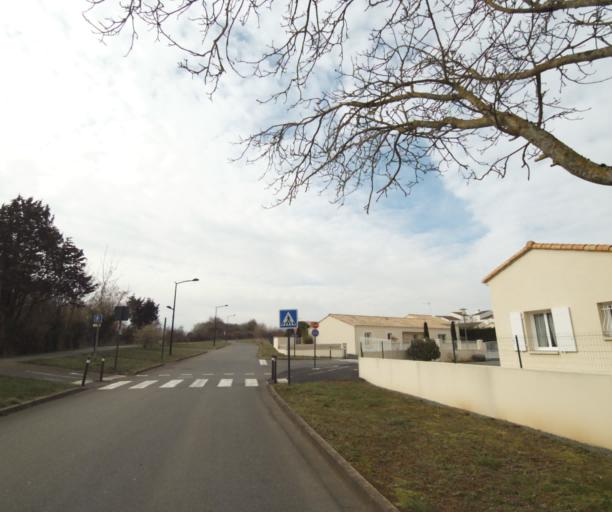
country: FR
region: Poitou-Charentes
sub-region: Departement des Deux-Sevres
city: Aiffres
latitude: 46.3135
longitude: -0.4300
